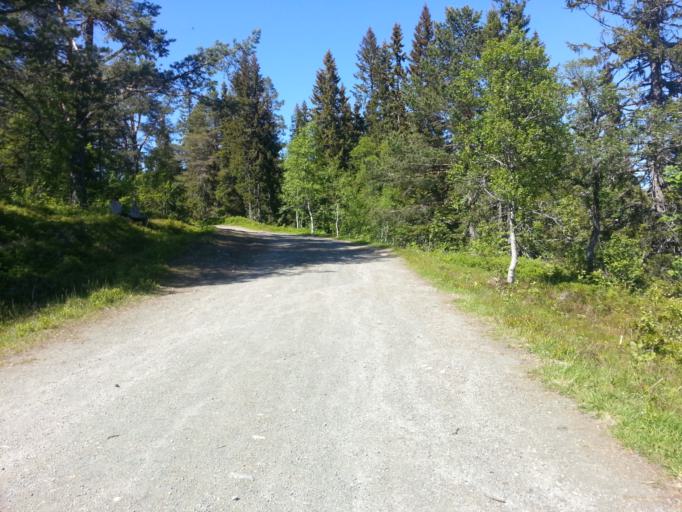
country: NO
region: Sor-Trondelag
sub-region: Trondheim
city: Trondheim
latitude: 63.4099
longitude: 10.2878
